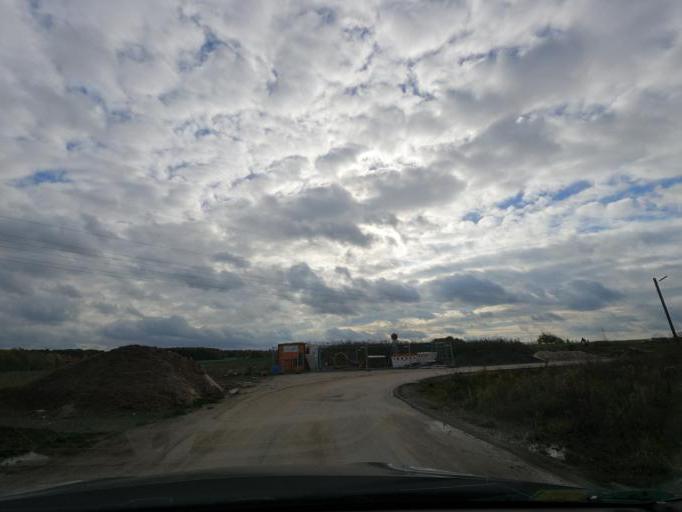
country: DE
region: Lower Saxony
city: Leiferde
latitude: 52.2027
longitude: 10.5238
